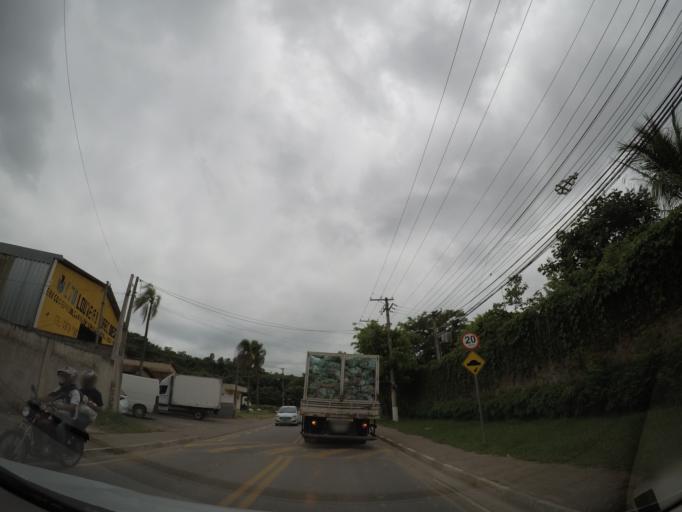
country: BR
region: Sao Paulo
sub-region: Louveira
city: Louveira
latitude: -23.0778
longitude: -46.9633
